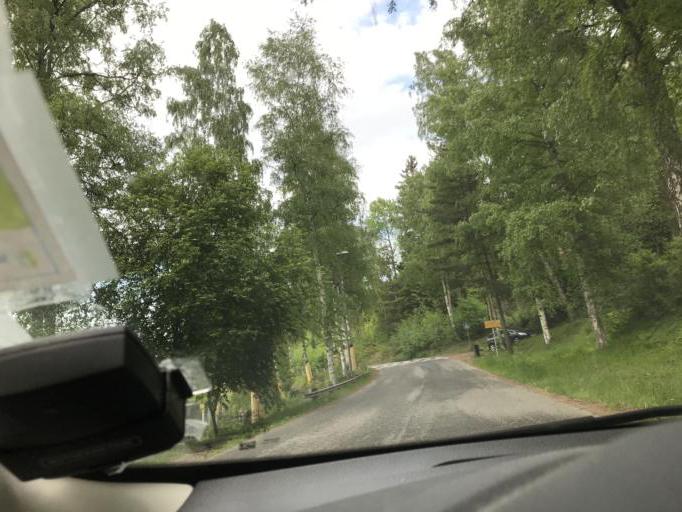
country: SE
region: Stockholm
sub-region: Botkyrka Kommun
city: Varsta
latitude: 59.1922
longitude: 17.7987
